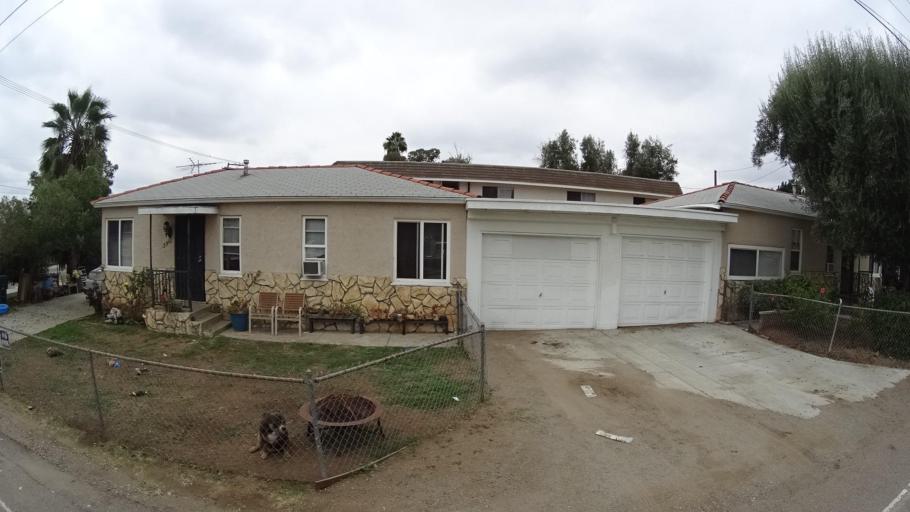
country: US
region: California
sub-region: San Diego County
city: Spring Valley
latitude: 32.7448
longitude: -116.9988
